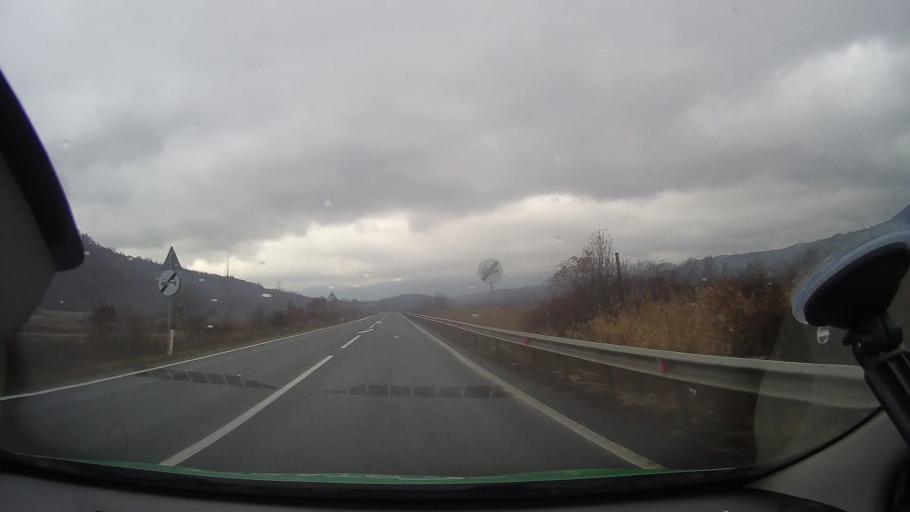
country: RO
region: Hunedoara
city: Vata de Jos
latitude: 46.2175
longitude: 22.5760
